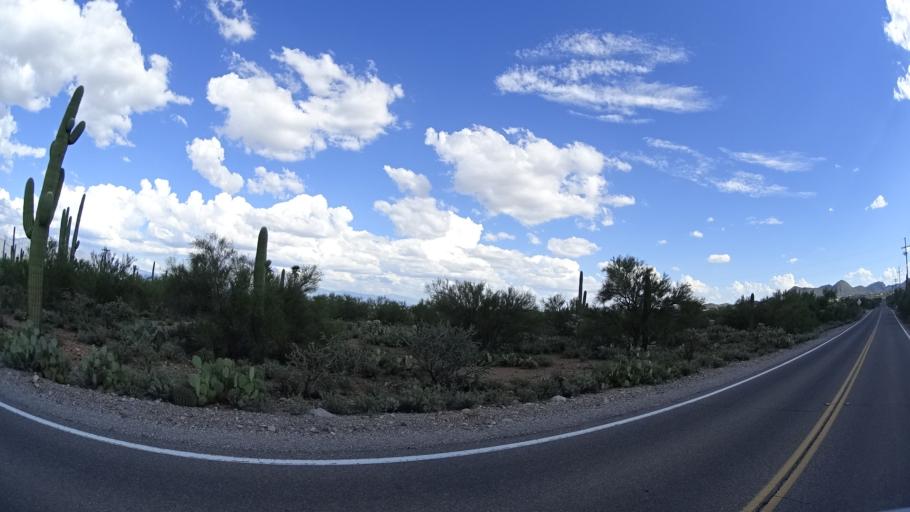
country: US
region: Arizona
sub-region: Pima County
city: Flowing Wells
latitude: 32.2712
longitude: -111.0629
